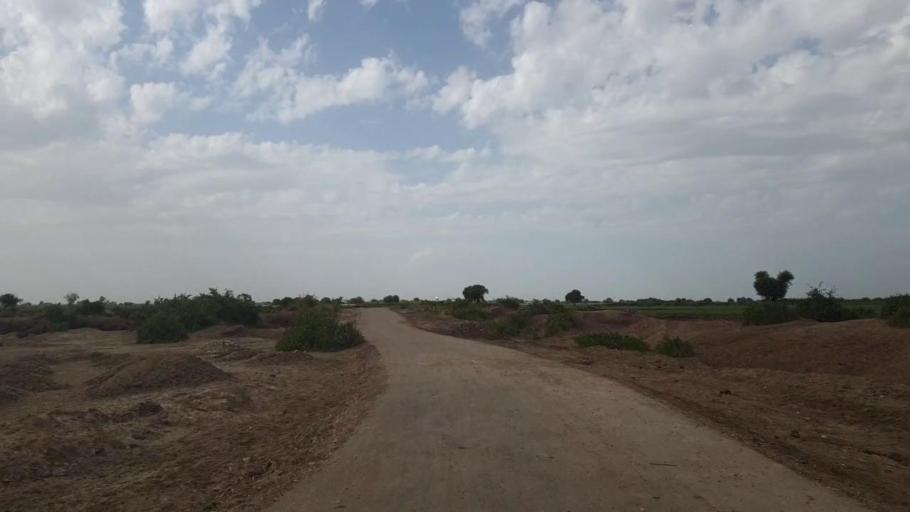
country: PK
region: Sindh
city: Hala
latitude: 25.9255
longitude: 68.4308
